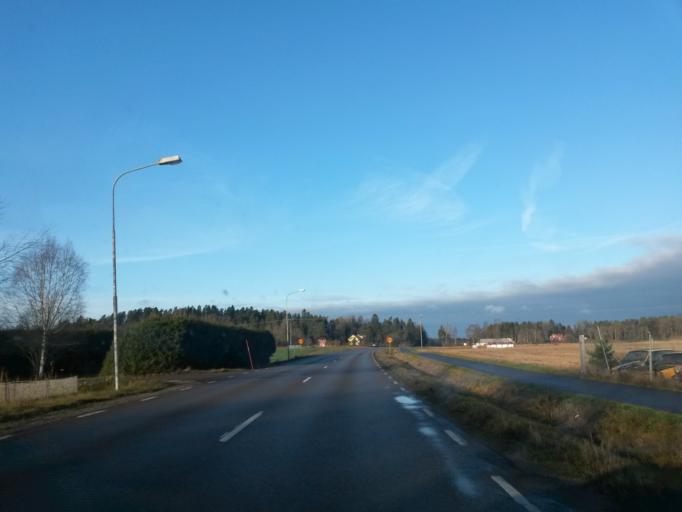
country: SE
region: Vaestra Goetaland
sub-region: Essunga Kommun
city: Nossebro
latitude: 58.1963
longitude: 12.7209
